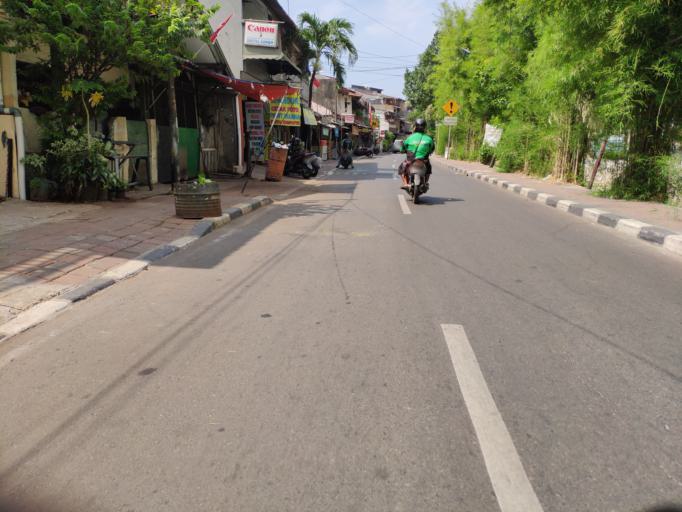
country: ID
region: Jakarta Raya
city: Jakarta
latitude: -6.2027
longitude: 106.8689
